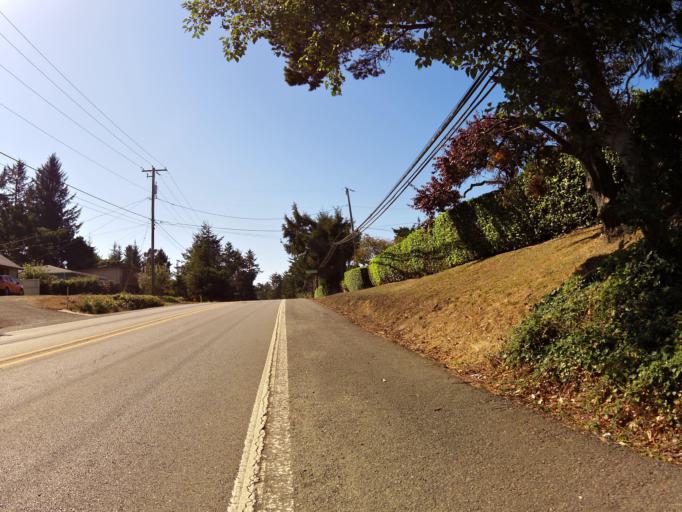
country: US
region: Oregon
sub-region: Coos County
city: Barview
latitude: 43.3574
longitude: -124.3094
